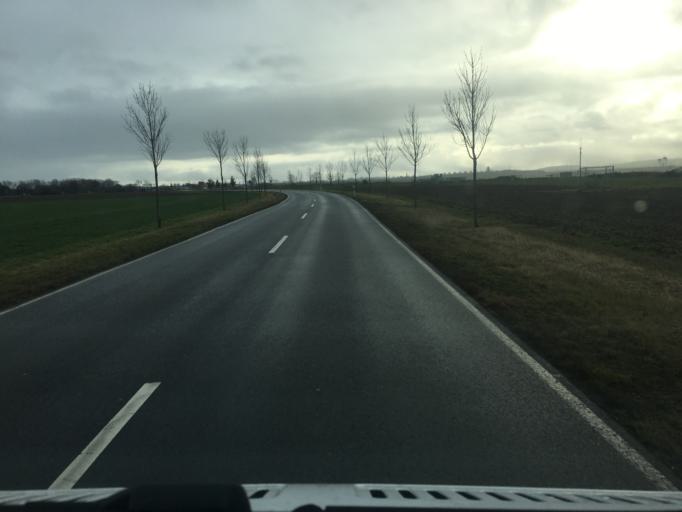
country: DE
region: North Rhine-Westphalia
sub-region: Regierungsbezirk Koln
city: Inden
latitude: 50.8686
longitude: 6.4051
